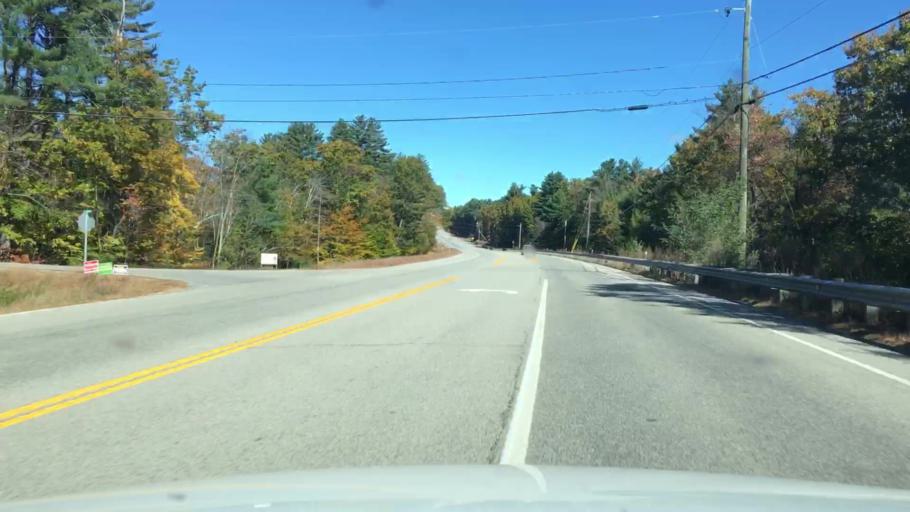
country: US
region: New Hampshire
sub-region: Carroll County
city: Wakefield
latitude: 43.5843
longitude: -71.0326
